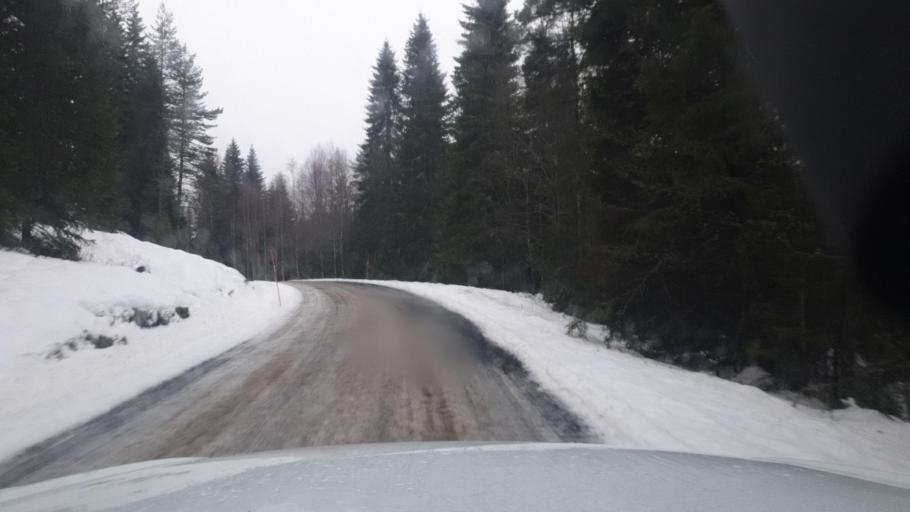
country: SE
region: Vaermland
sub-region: Eda Kommun
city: Charlottenberg
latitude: 60.1416
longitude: 12.5962
